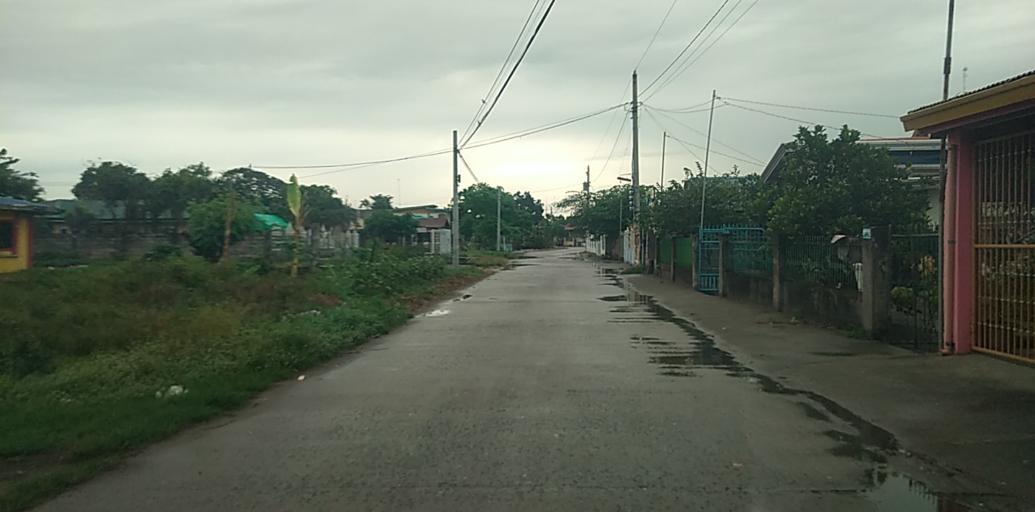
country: PH
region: Central Luzon
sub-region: Province of Pampanga
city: Arayat
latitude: 15.1405
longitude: 120.7354
